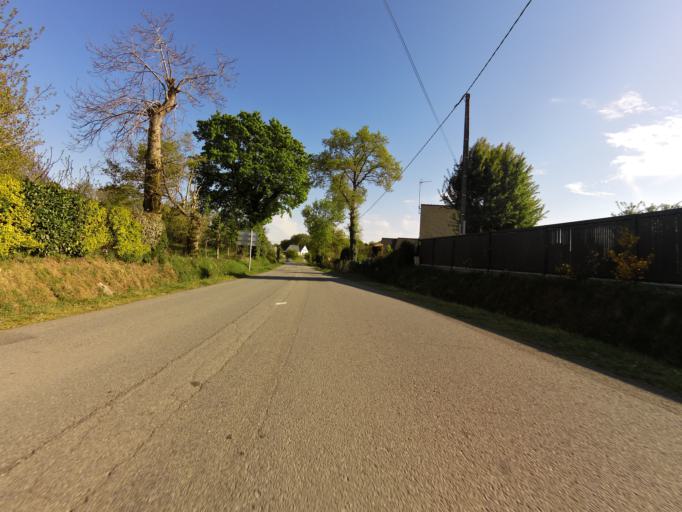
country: FR
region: Brittany
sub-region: Departement du Morbihan
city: Limerzel
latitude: 47.6415
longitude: -2.3605
